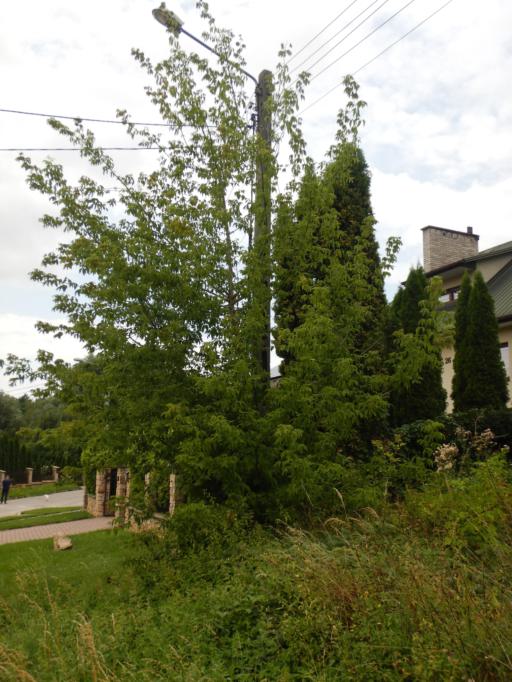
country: PL
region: Swietokrzyskie
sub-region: Powiat opatowski
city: Opatow
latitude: 50.7950
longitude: 21.4306
